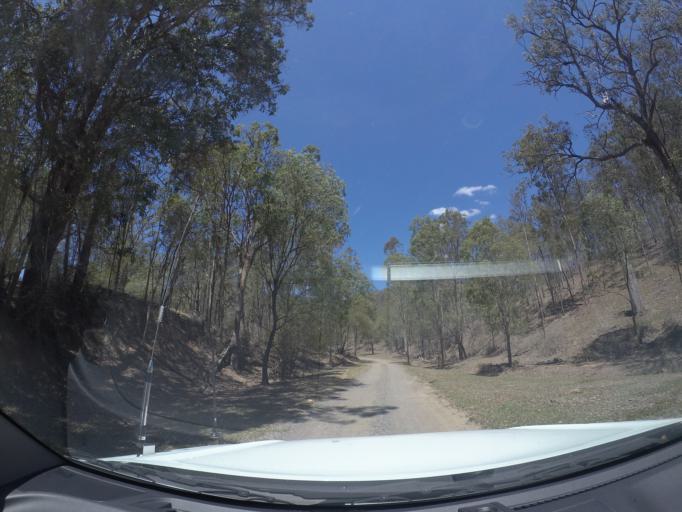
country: AU
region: Queensland
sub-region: Ipswich
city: Deebing Heights
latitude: -27.7628
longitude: 152.8077
